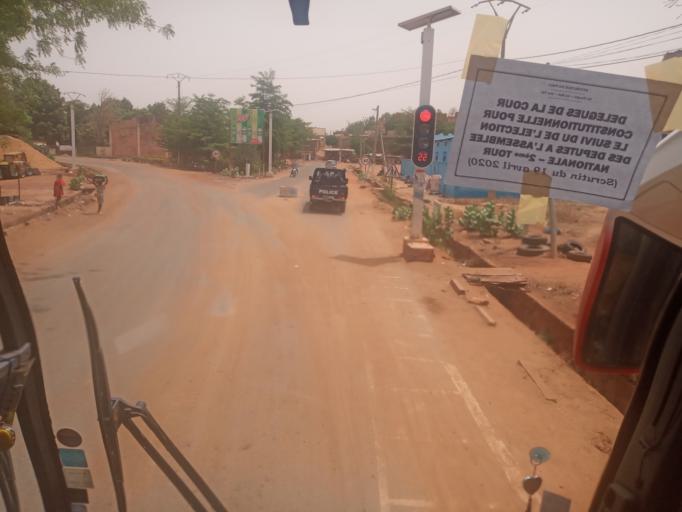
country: ML
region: Koulikoro
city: Koulikoro
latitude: 12.8745
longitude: -7.5501
